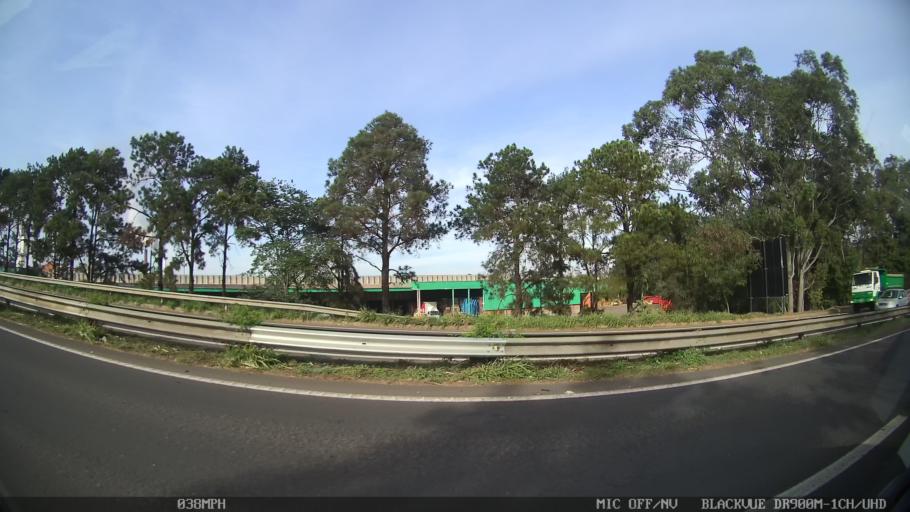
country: BR
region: Sao Paulo
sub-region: Piracicaba
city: Piracicaba
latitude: -22.6854
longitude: -47.6756
